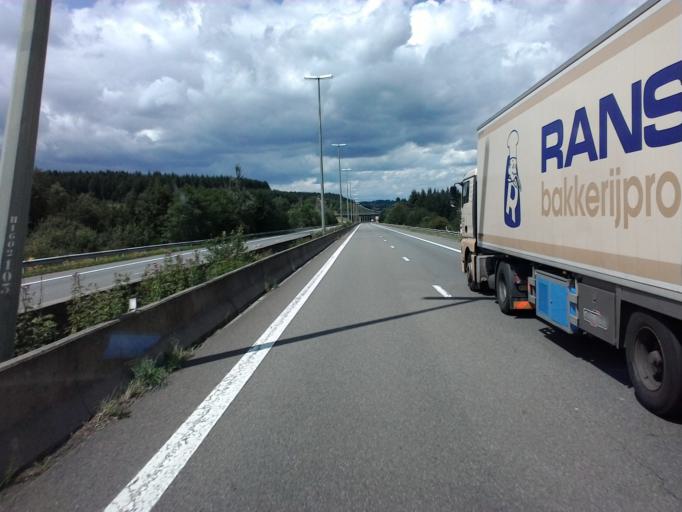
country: BE
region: Wallonia
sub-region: Province du Luxembourg
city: Manhay
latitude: 50.3393
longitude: 5.6930
